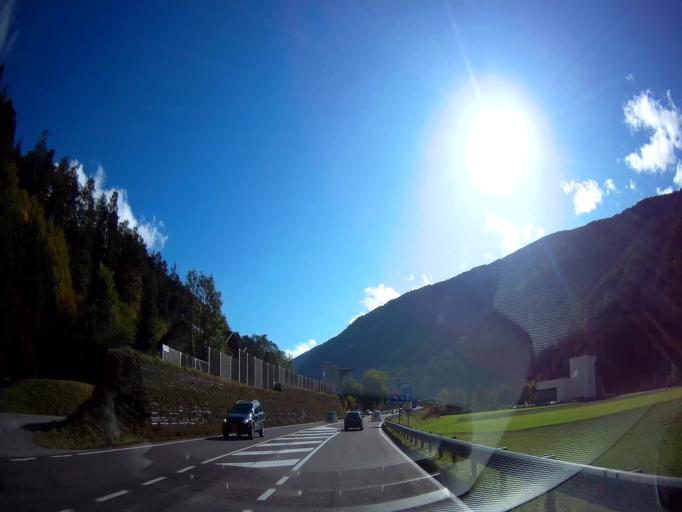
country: IT
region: Trentino-Alto Adige
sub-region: Bolzano
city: Vandoies - Vintl
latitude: 46.8170
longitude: 11.7126
